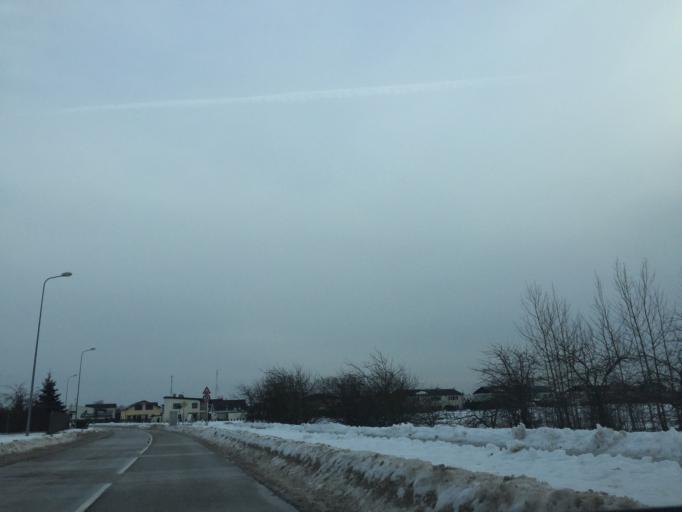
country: LV
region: Ikskile
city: Ikskile
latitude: 56.8391
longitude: 24.4745
